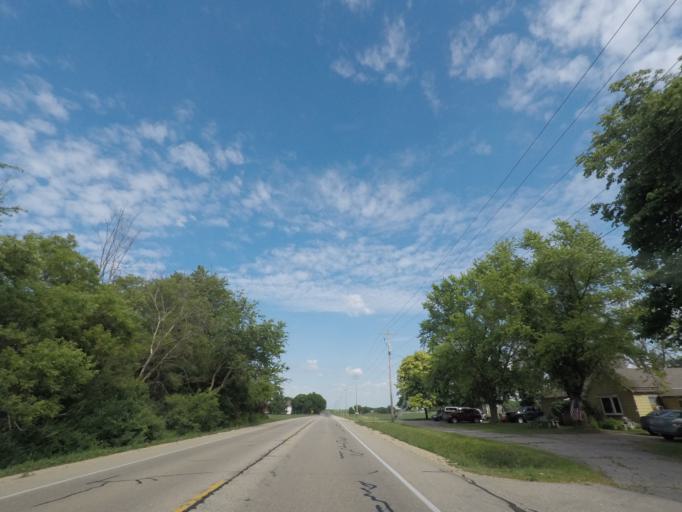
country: US
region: Wisconsin
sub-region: Jefferson County
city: Palmyra
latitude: 42.7967
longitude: -88.6324
